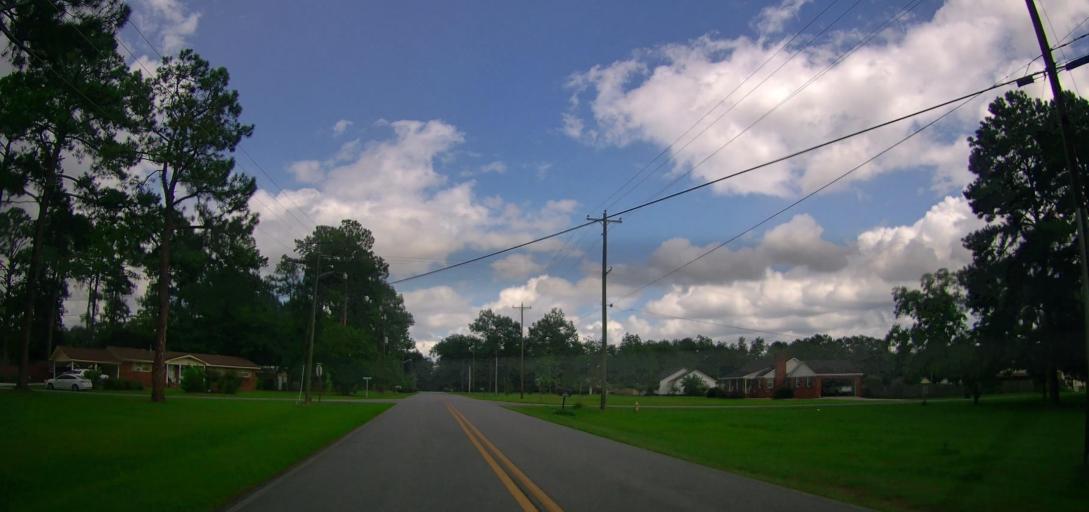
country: US
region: Georgia
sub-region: Ben Hill County
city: Fitzgerald
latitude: 31.7055
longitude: -83.2825
